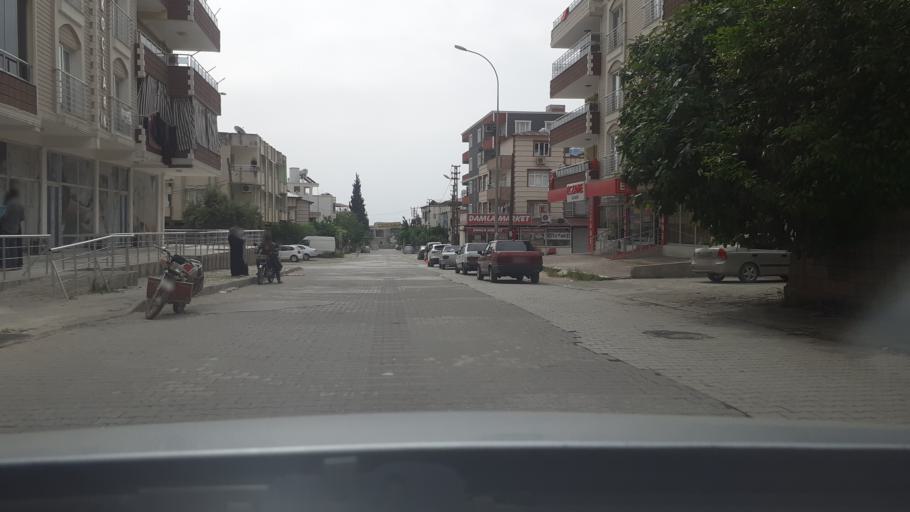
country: TR
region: Hatay
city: Kirikhan
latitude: 36.4951
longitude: 36.3640
